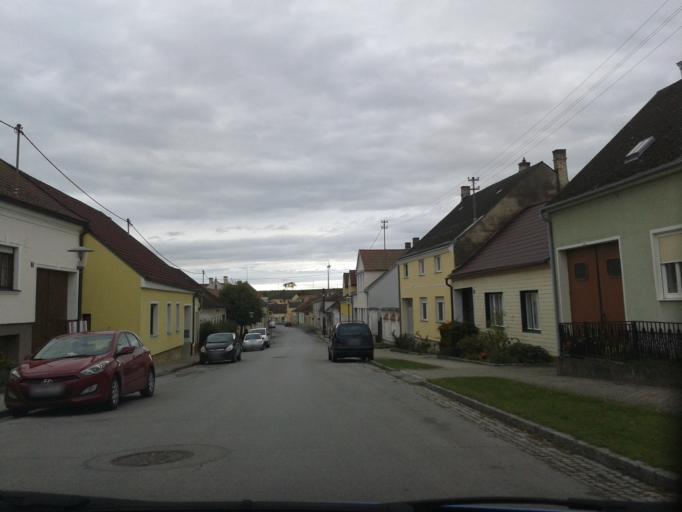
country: AT
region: Lower Austria
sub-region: Politischer Bezirk Mistelbach
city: Altlichtenwarth
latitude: 48.6469
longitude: 16.7959
